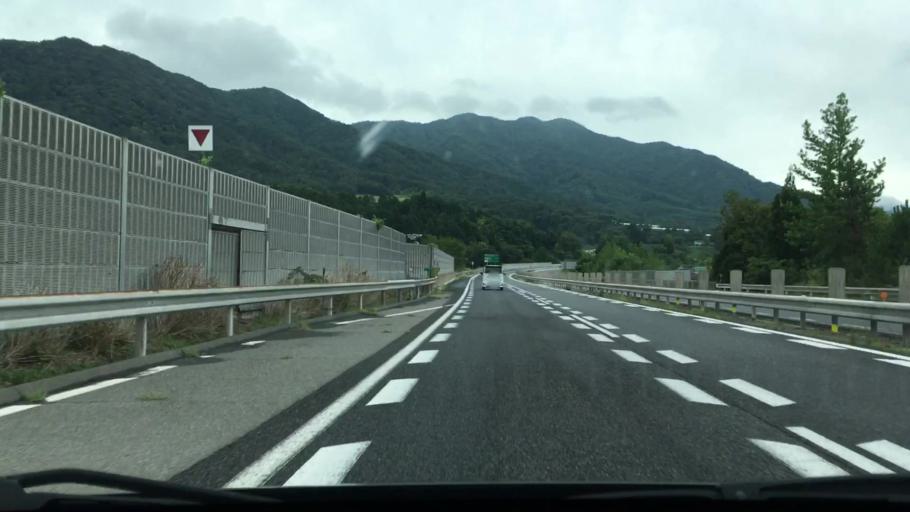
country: JP
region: Hiroshima
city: Hiroshima-shi
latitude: 34.6473
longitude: 132.5168
